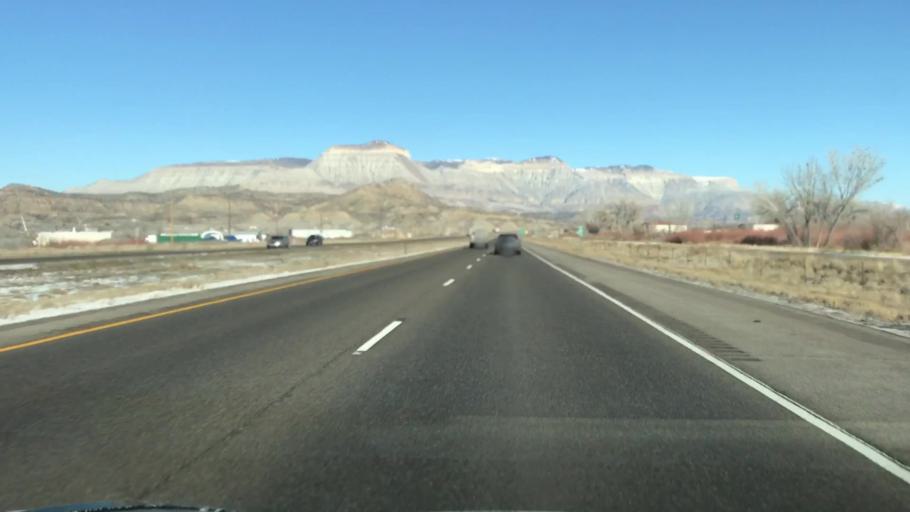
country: US
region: Colorado
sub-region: Garfield County
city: Parachute
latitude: 39.3155
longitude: -108.2123
